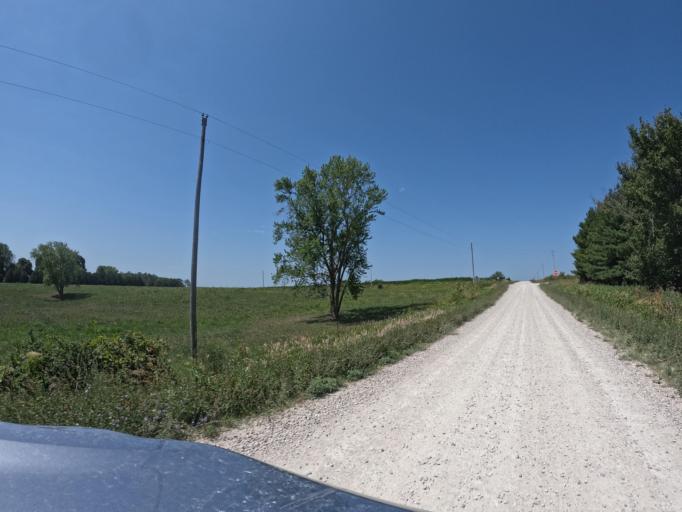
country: US
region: Iowa
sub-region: Henry County
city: Mount Pleasant
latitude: 40.8791
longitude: -91.5593
